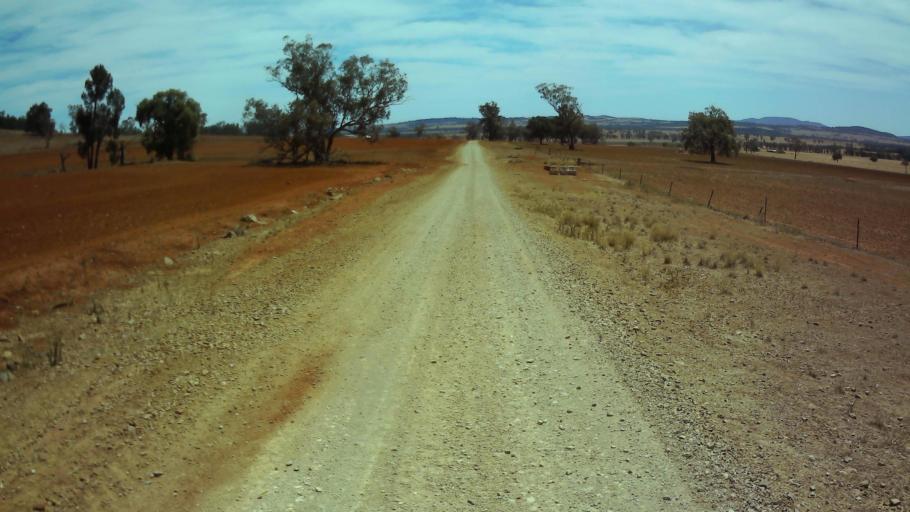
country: AU
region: New South Wales
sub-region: Weddin
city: Grenfell
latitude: -33.7486
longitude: 148.1645
